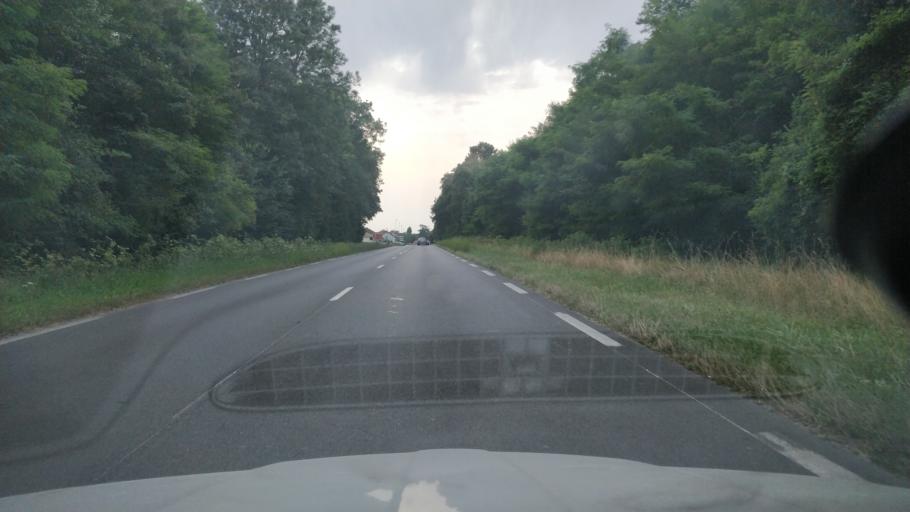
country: FR
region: Ile-de-France
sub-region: Departement de Seine-et-Marne
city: Vaires-sur-Marne
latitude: 48.8829
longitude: 2.6407
